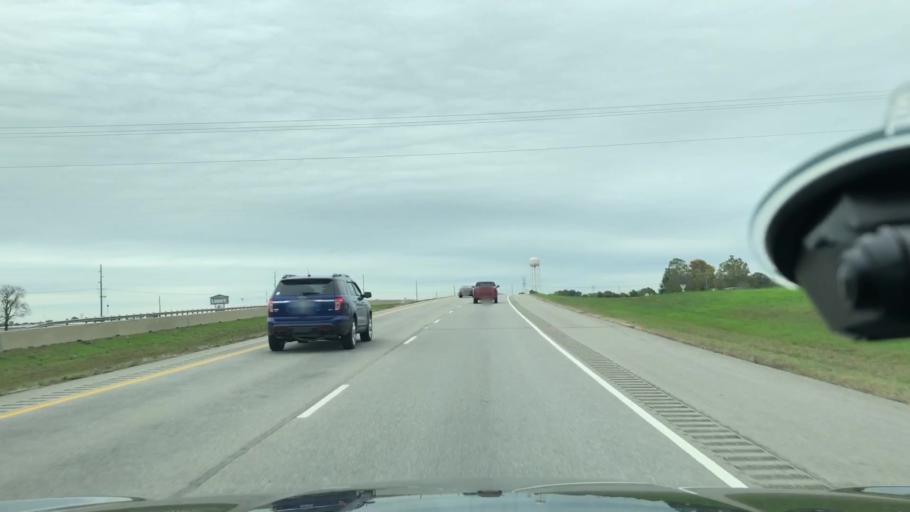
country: US
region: Texas
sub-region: Franklin County
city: Mount Vernon
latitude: 33.1620
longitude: -95.1787
